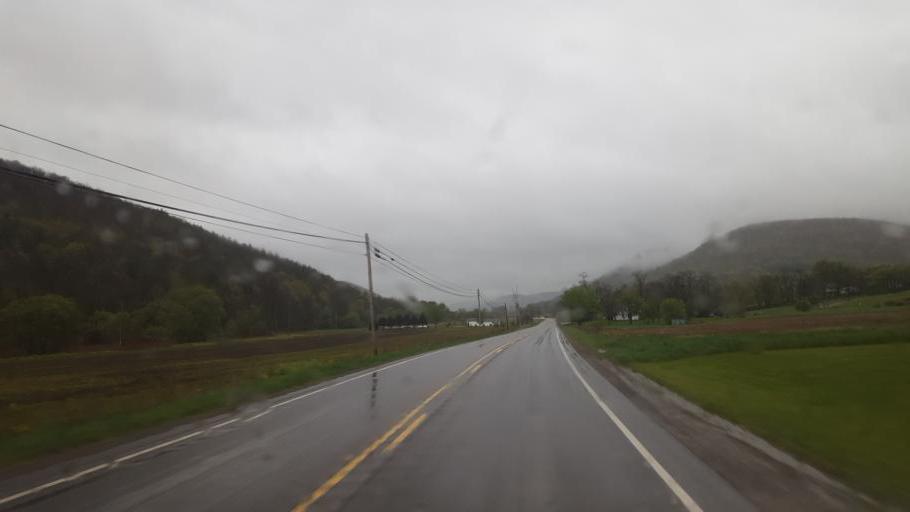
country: US
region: Pennsylvania
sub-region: Tioga County
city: Westfield
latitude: 41.9131
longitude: -77.5897
